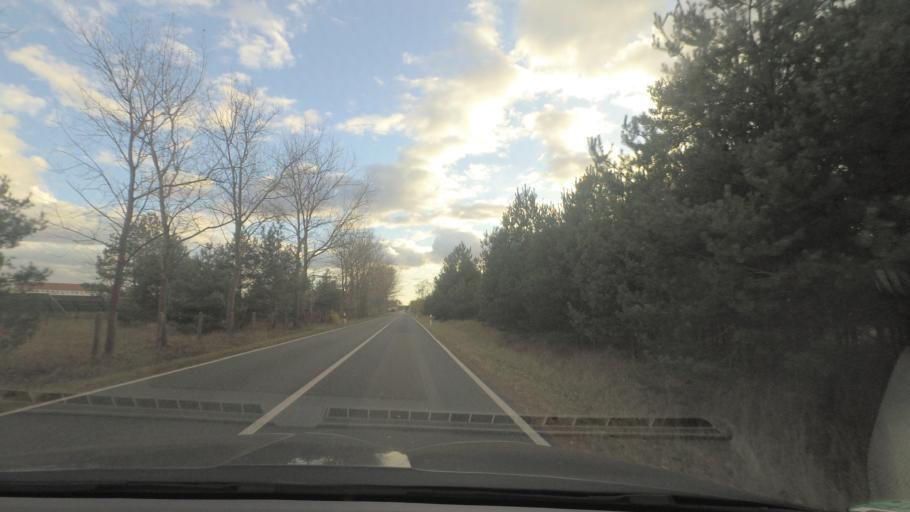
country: DE
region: Brandenburg
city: Sperenberg
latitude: 52.0843
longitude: 13.3228
